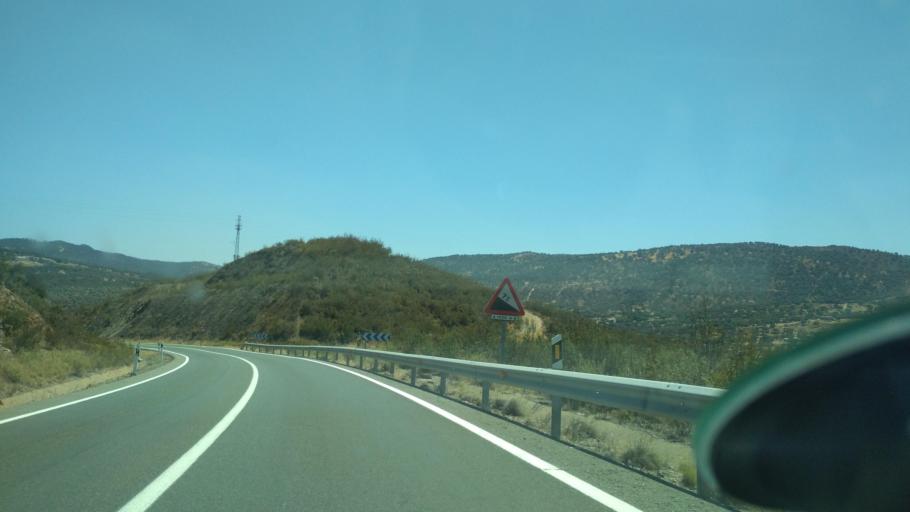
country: ES
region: Andalusia
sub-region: Provincia de Huelva
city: Campofrio
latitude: 37.8048
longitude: -6.5522
